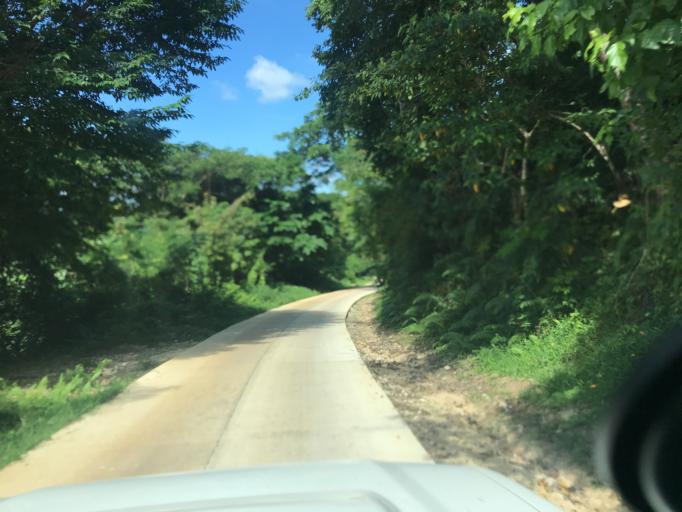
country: VU
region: Sanma
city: Luganville
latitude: -15.5266
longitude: 167.1493
